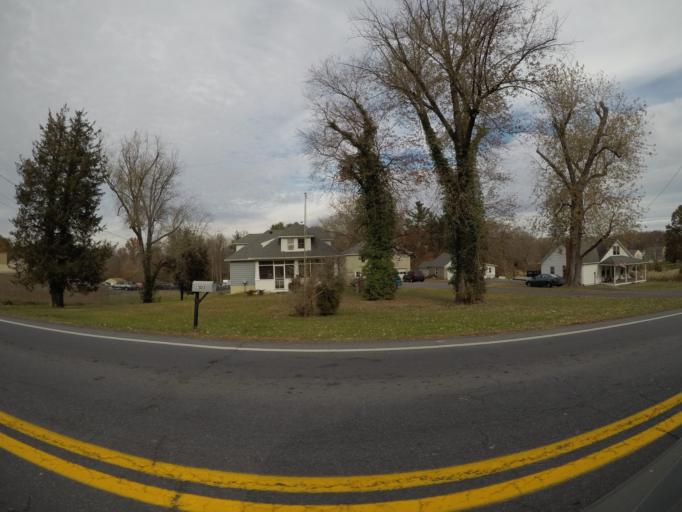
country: US
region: Maryland
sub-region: Harford County
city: Riverside
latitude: 39.4616
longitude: -76.2760
